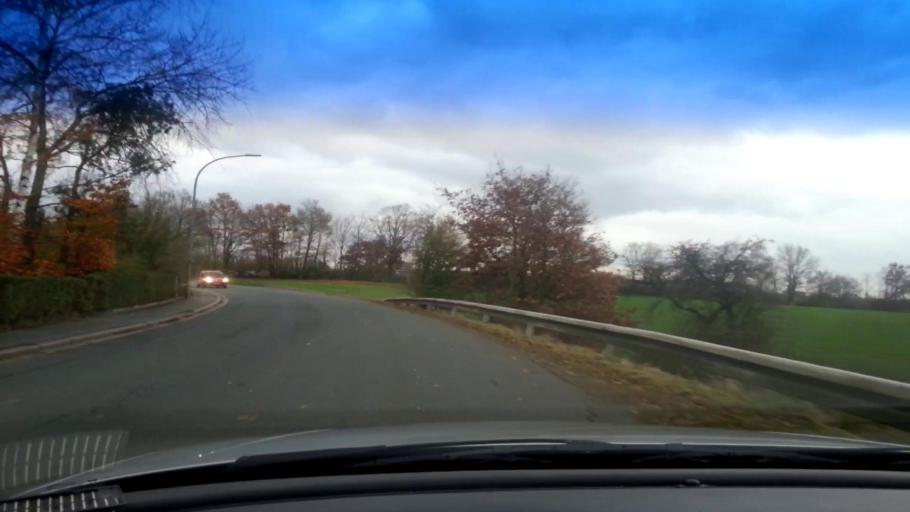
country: DE
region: Bavaria
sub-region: Upper Franconia
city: Stegaurach
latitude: 49.8761
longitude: 10.8623
